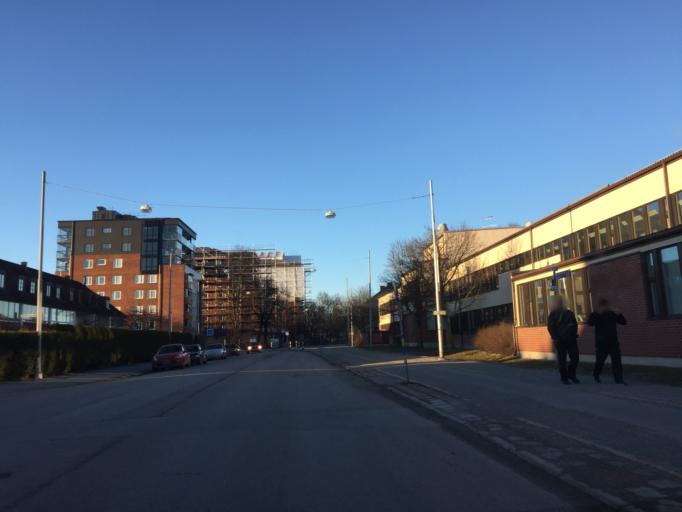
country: SE
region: OErebro
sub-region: Orebro Kommun
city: Orebro
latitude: 59.2838
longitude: 15.2207
